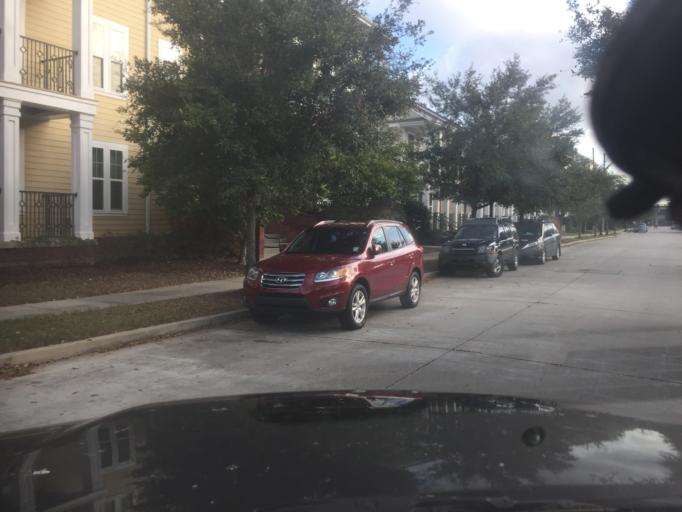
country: US
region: Louisiana
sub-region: Orleans Parish
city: New Orleans
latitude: 29.9961
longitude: -90.0782
